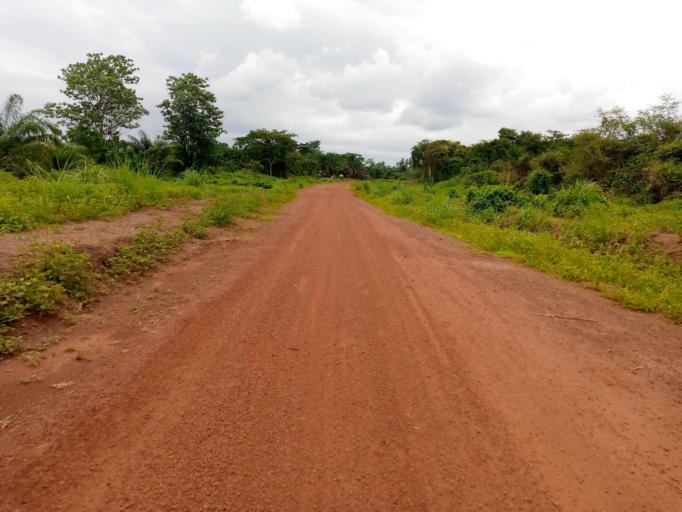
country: SL
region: Southern Province
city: Moyamba
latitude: 8.0842
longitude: -12.4506
